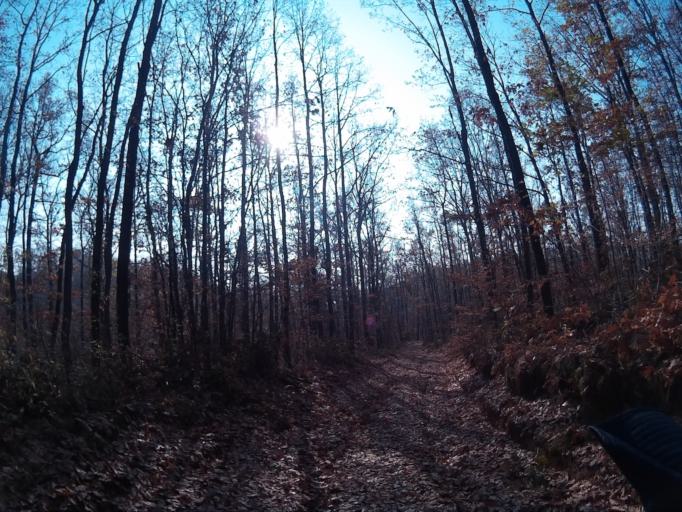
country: HU
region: Heves
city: Felsotarkany
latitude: 47.9985
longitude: 20.3855
